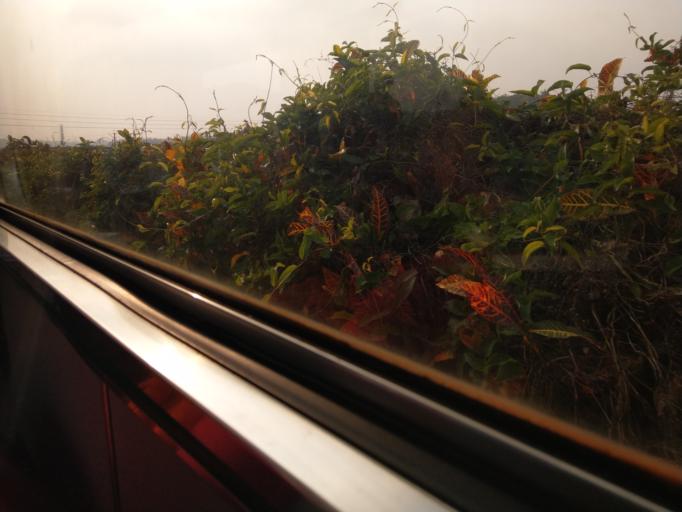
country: TW
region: Taiwan
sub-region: Chiayi
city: Jiayi Shi
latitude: 23.5032
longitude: 120.5299
